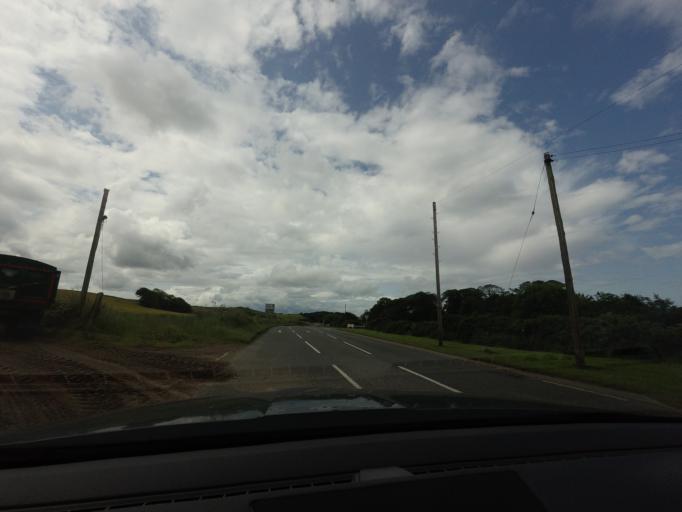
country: GB
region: Scotland
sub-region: Aberdeenshire
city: Whitehills
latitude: 57.6645
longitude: -2.5628
